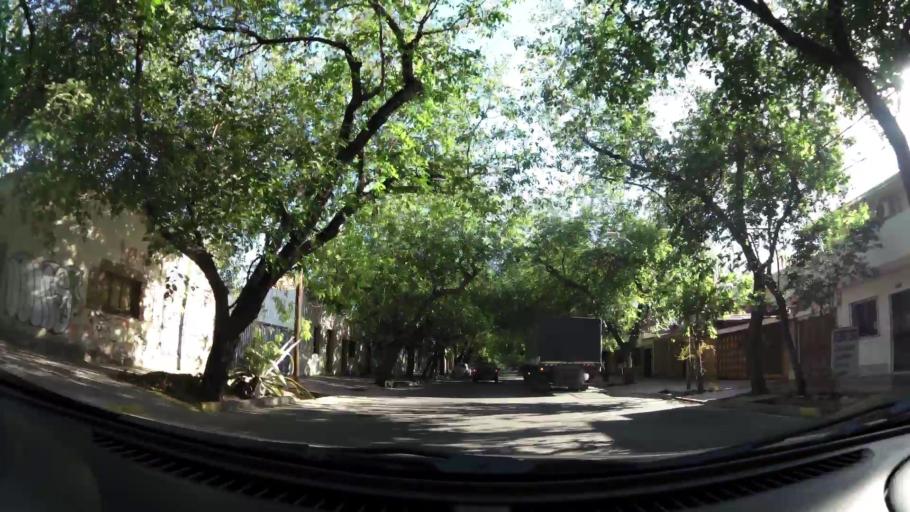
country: AR
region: Mendoza
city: Mendoza
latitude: -32.8724
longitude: -68.8373
